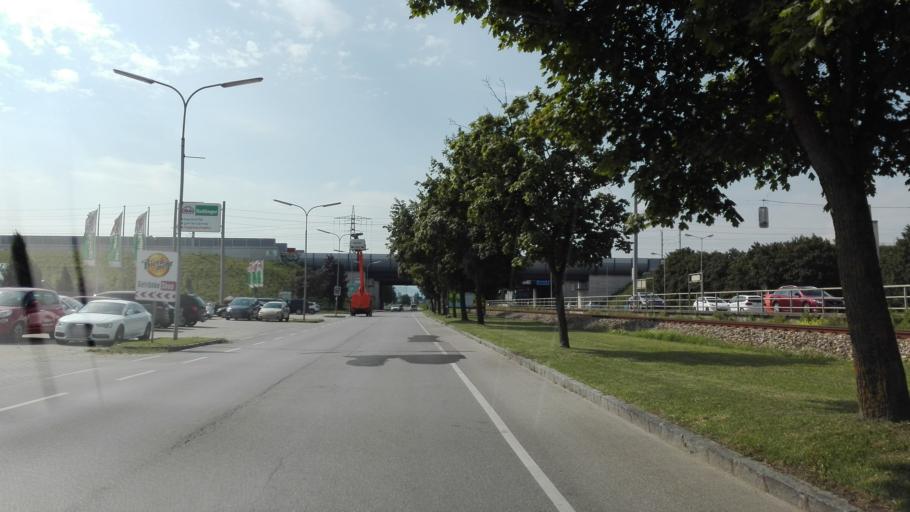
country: AT
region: Lower Austria
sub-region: Sankt Polten Stadt
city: Sankt Poelten
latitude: 48.1789
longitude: 15.6163
